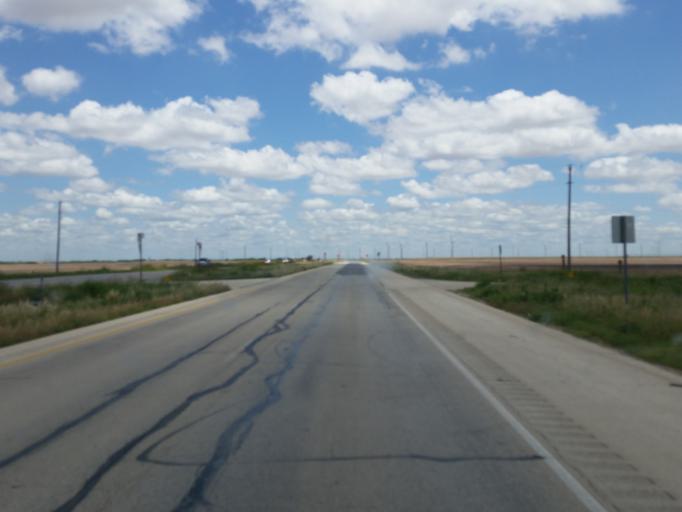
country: US
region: Texas
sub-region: Nolan County
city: Roscoe
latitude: 32.4791
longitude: -100.6167
